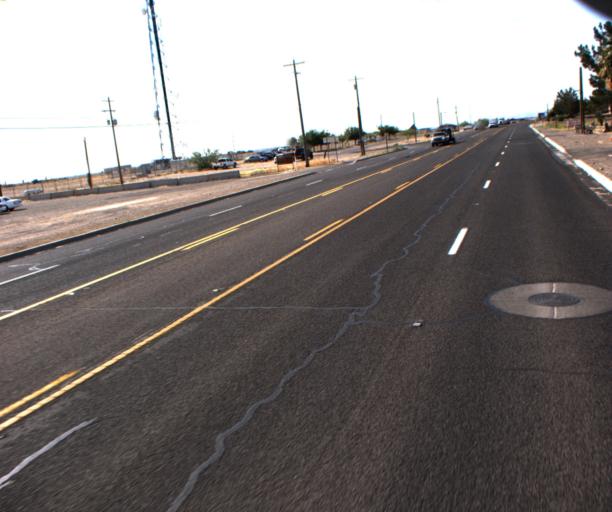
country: US
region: Arizona
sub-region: Graham County
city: Cactus Flat
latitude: 32.7951
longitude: -109.7078
